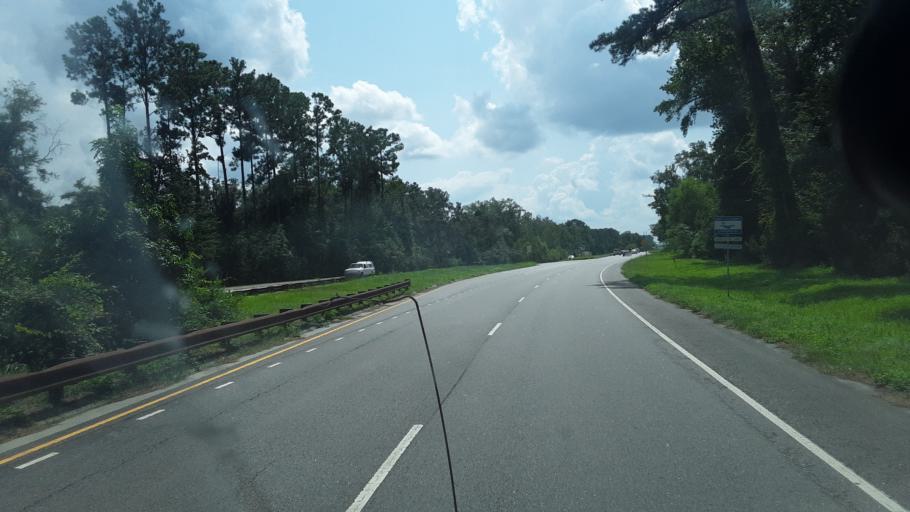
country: US
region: South Carolina
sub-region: Beaufort County
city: Bluffton
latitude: 32.2756
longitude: -80.9476
